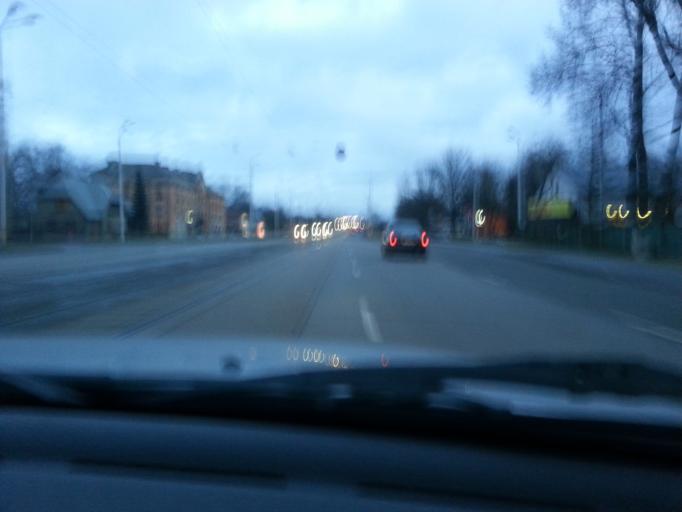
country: LV
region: Marupe
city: Marupe
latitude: 56.9520
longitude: 24.0373
